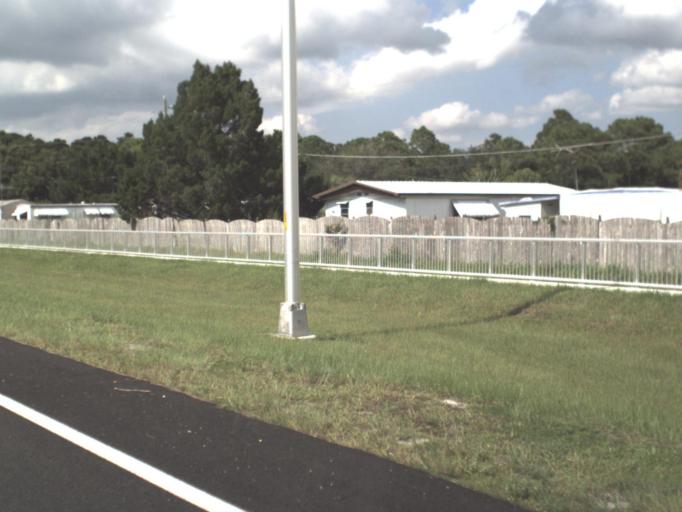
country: US
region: Florida
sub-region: Sarasota County
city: Warm Mineral Springs
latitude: 27.0429
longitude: -82.3010
